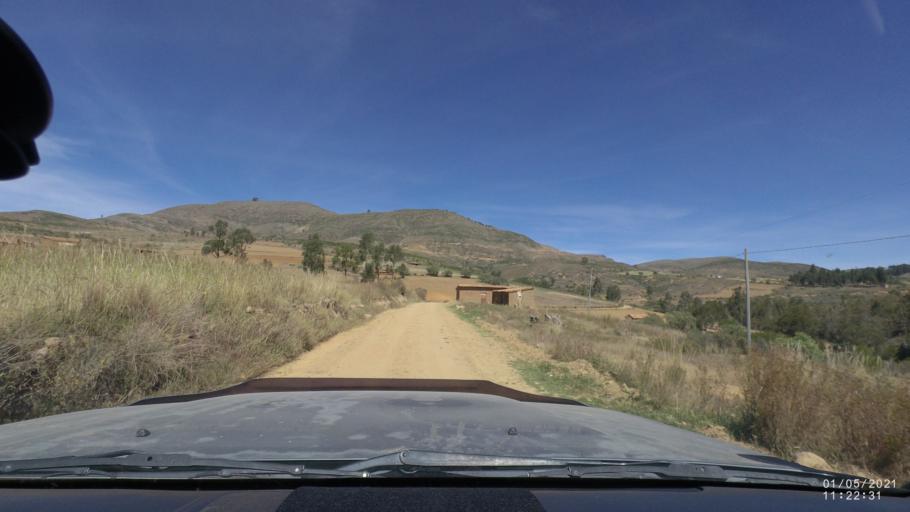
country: BO
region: Cochabamba
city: Tarata
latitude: -17.6497
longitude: -66.1316
